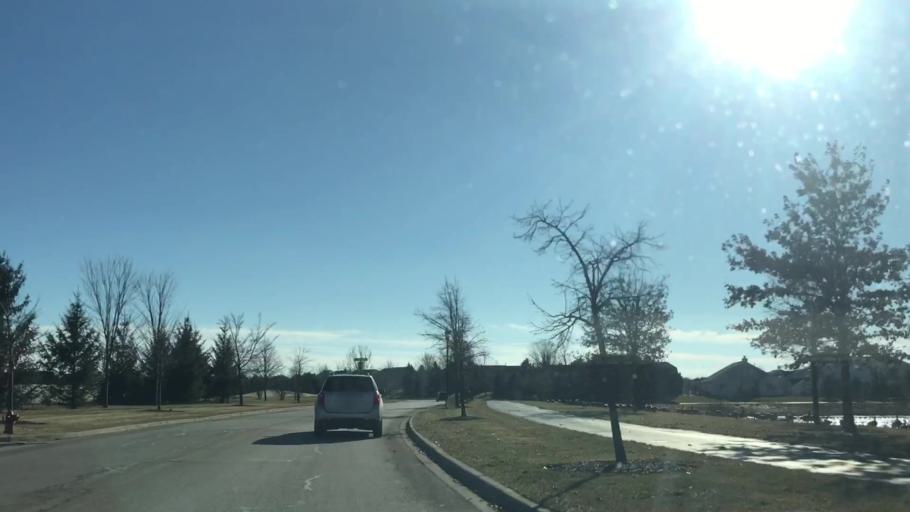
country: US
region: Illinois
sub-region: Kane County
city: Pingree Grove
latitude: 42.0830
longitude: -88.4316
